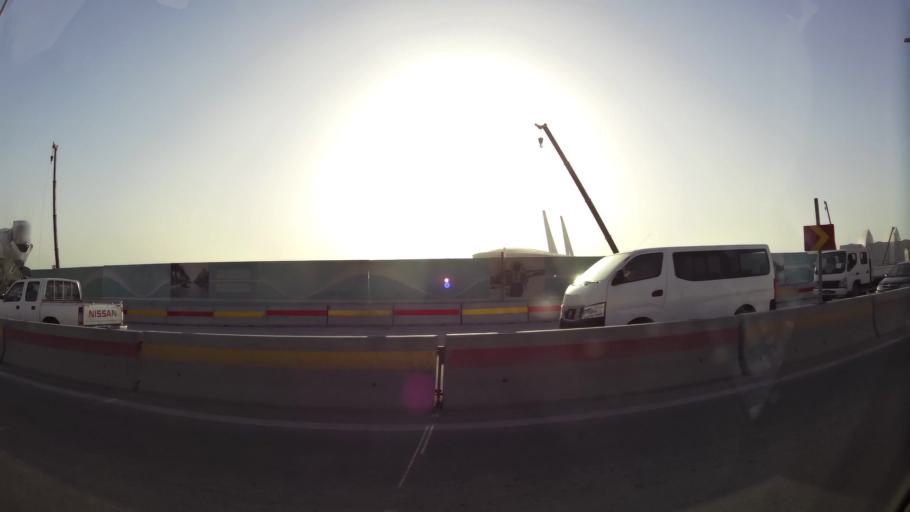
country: QA
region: Baladiyat ar Rayyan
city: Ar Rayyan
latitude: 25.3168
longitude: 51.4503
